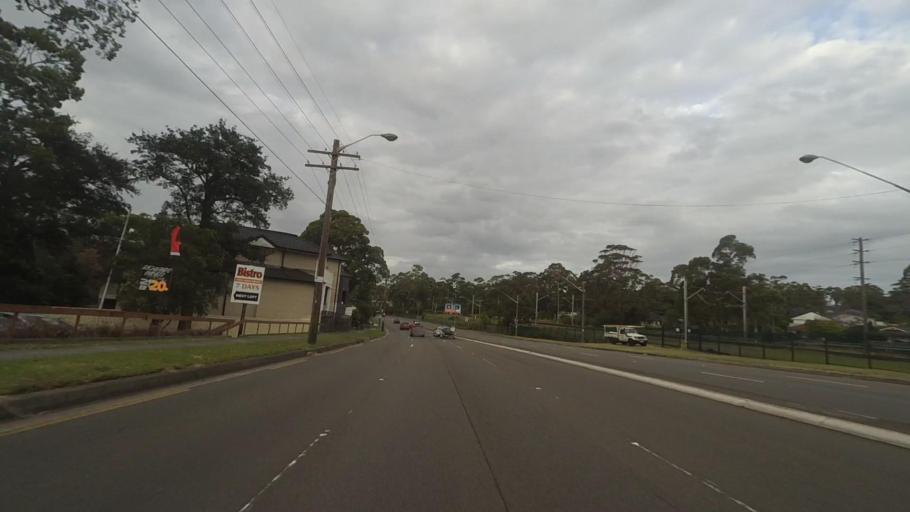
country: AU
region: New South Wales
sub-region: Sutherland Shire
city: Heathcote
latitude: -34.0861
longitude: 151.0094
